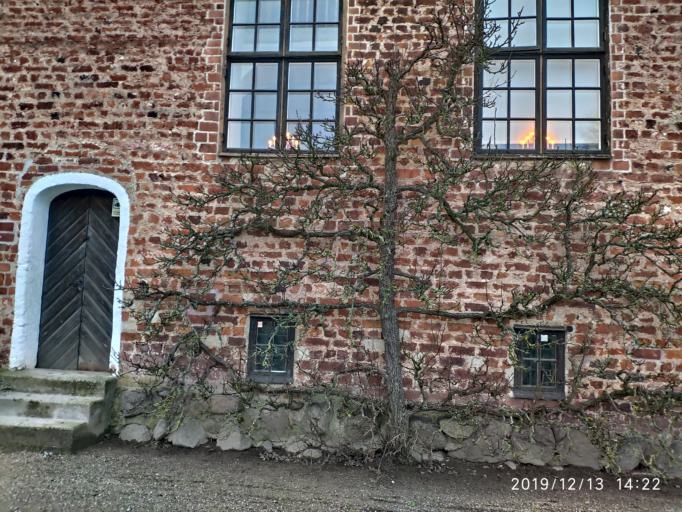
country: SE
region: Skane
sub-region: Skurups Kommun
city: Skurup
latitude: 55.5008
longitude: 13.4784
